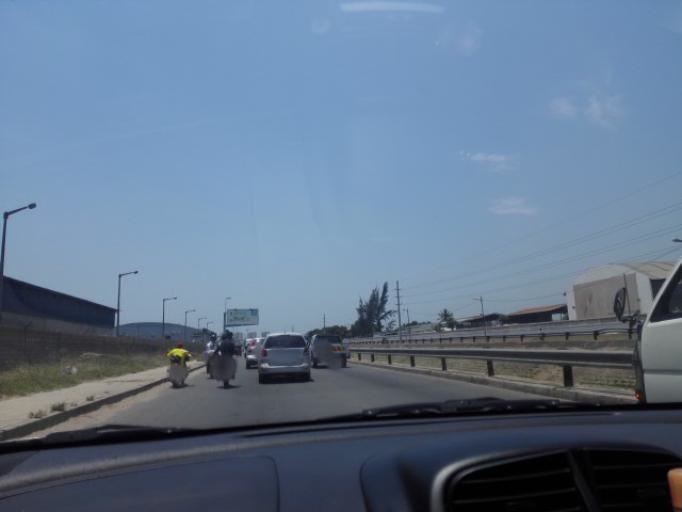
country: MZ
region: Maputo City
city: Maputo
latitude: -25.9408
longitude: 32.5701
